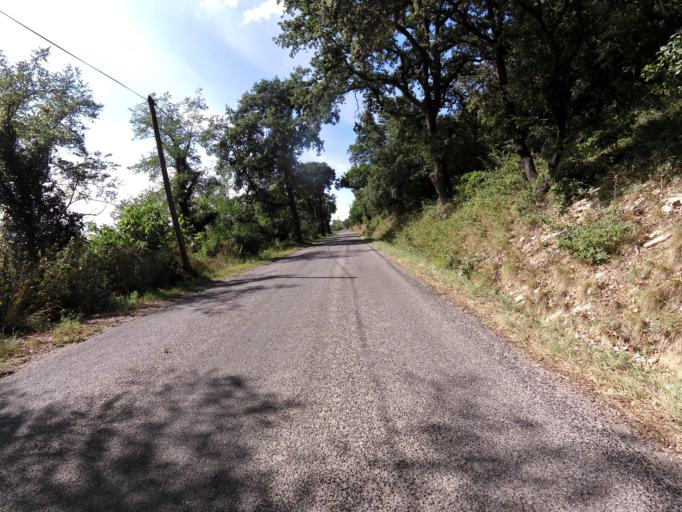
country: FR
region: Languedoc-Roussillon
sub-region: Departement du Gard
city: Lezan
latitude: 43.9781
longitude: 4.0188
